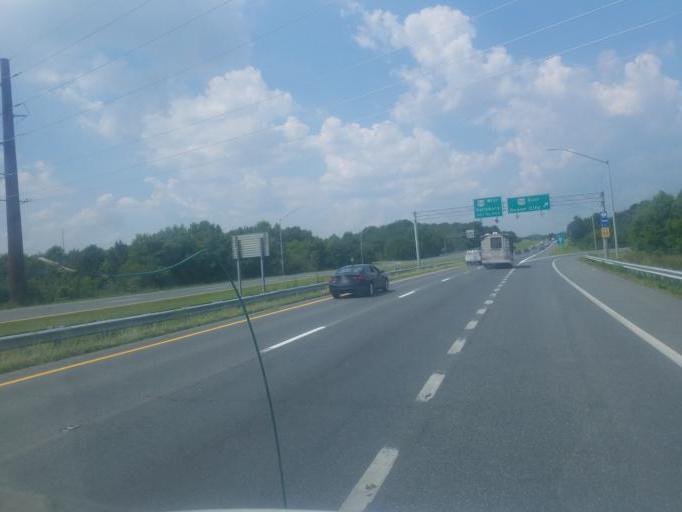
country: US
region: Maryland
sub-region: Worcester County
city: Berlin
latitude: 38.3381
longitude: -75.2121
